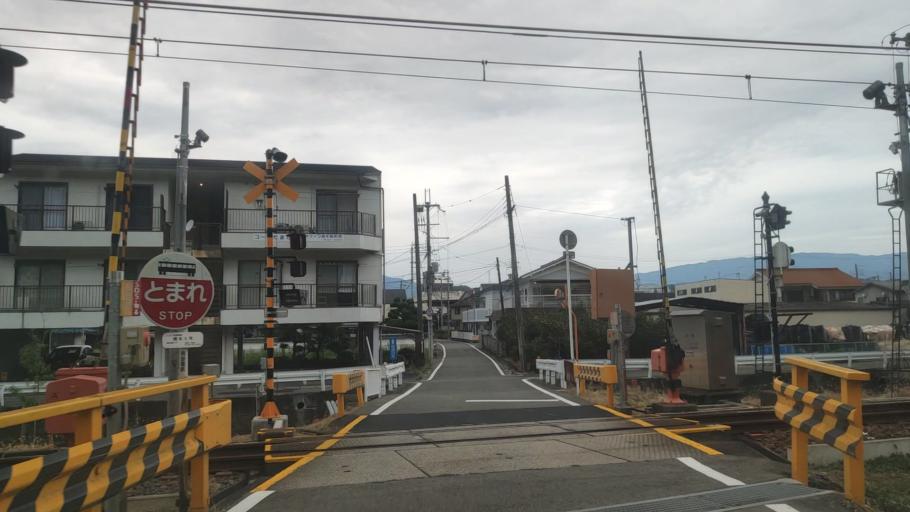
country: JP
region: Wakayama
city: Hashimoto
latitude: 34.3106
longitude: 135.6145
